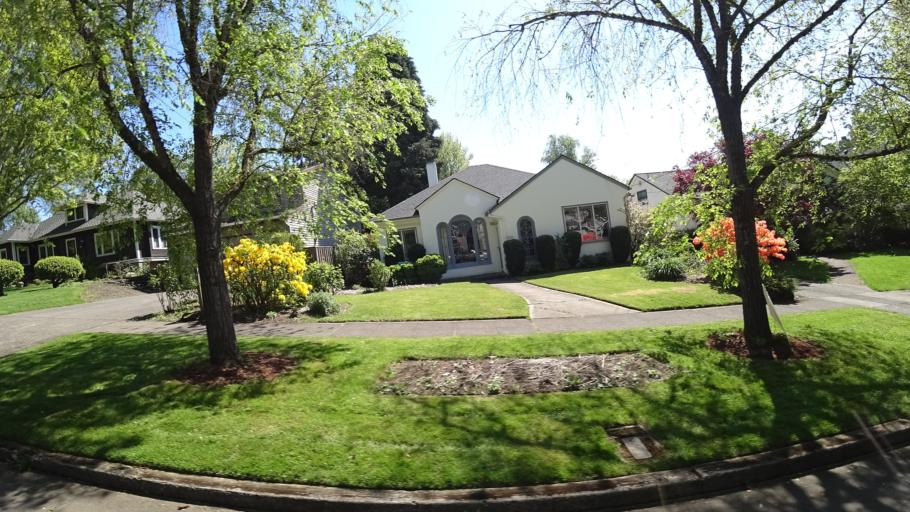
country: US
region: Oregon
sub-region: Clackamas County
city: Milwaukie
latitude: 45.4778
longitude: -122.6257
